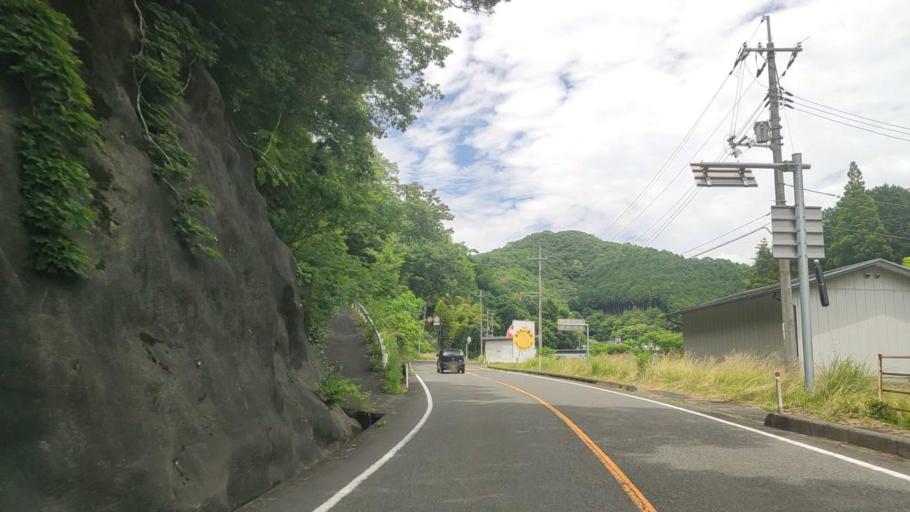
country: JP
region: Hyogo
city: Yamazakicho-nakabirose
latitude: 35.1110
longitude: 134.3281
